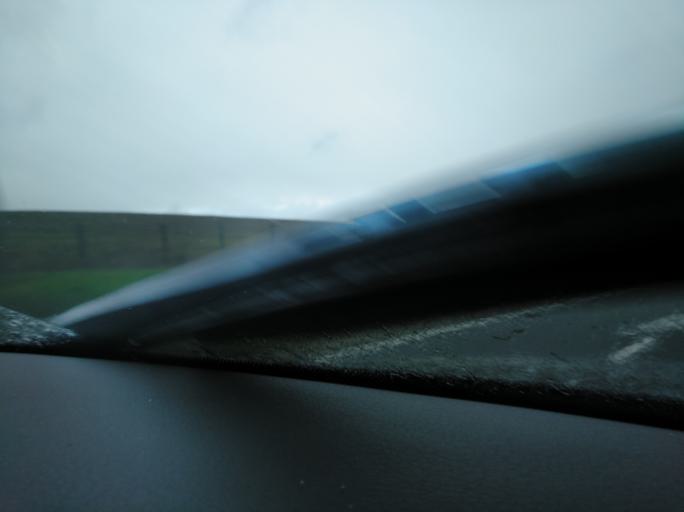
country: PT
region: Beja
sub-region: Castro Verde
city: Castro Verde
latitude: 37.7091
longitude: -7.9159
